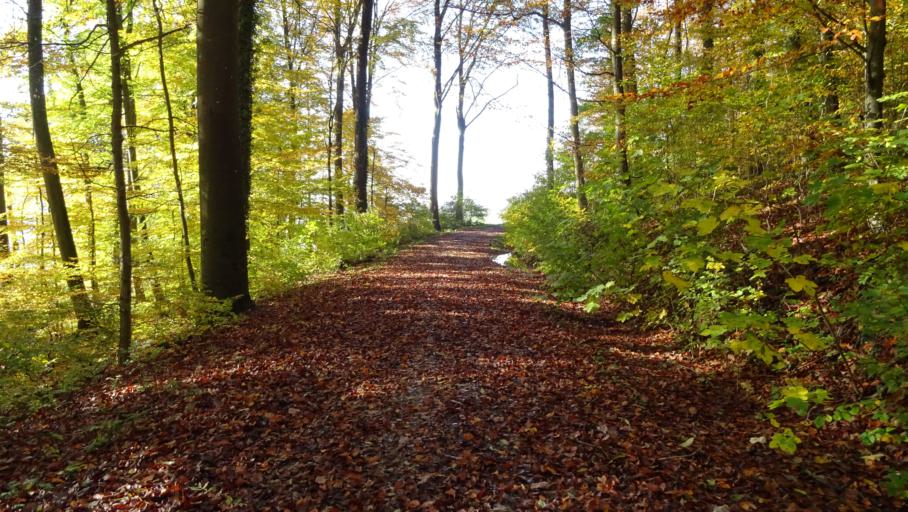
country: DE
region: Baden-Wuerttemberg
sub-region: Karlsruhe Region
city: Obrigheim
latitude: 49.3753
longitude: 9.0947
